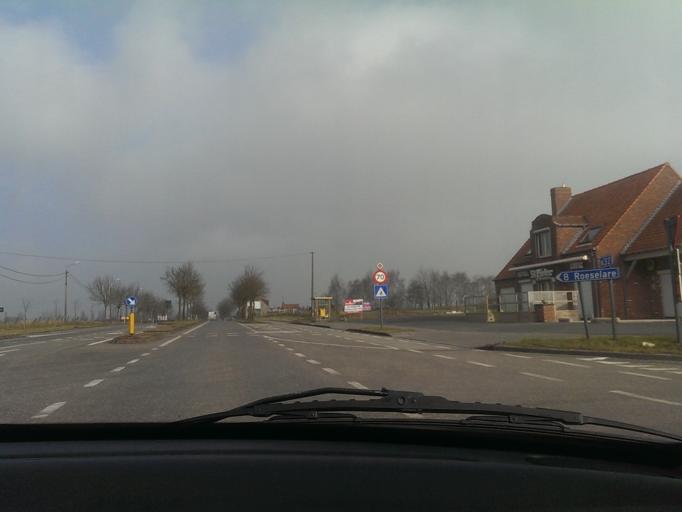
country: BE
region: Flanders
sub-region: Provincie West-Vlaanderen
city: Ledegem
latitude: 50.8751
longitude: 3.1118
